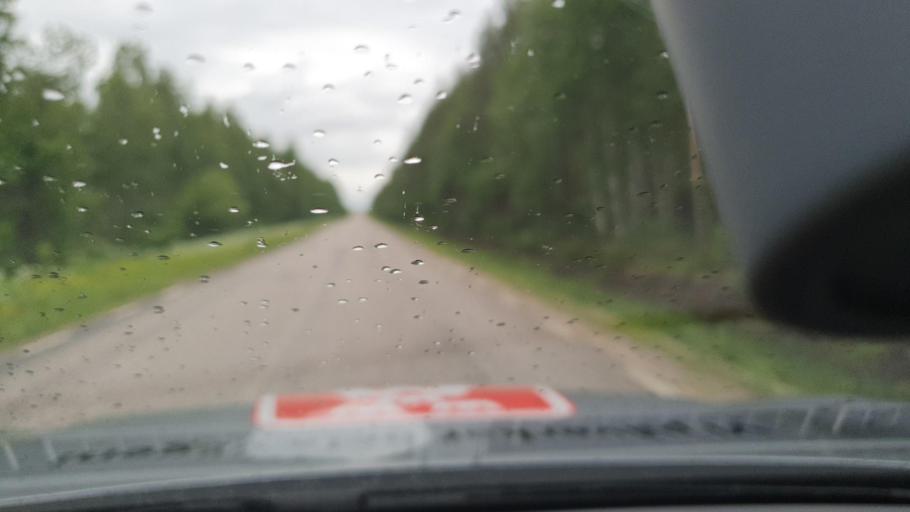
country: SE
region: Norrbotten
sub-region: Overkalix Kommun
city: OEverkalix
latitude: 66.3704
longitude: 22.8003
